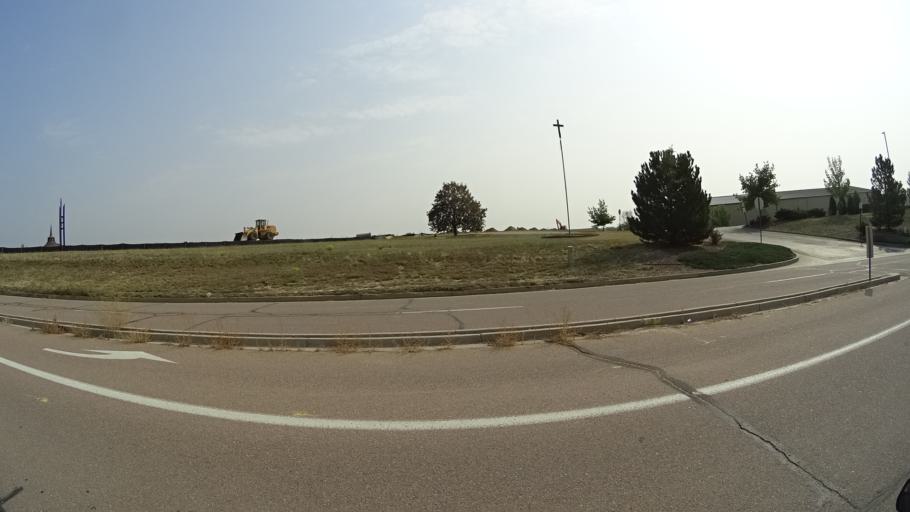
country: US
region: Colorado
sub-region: El Paso County
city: Stratmoor
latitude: 38.8152
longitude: -104.7526
